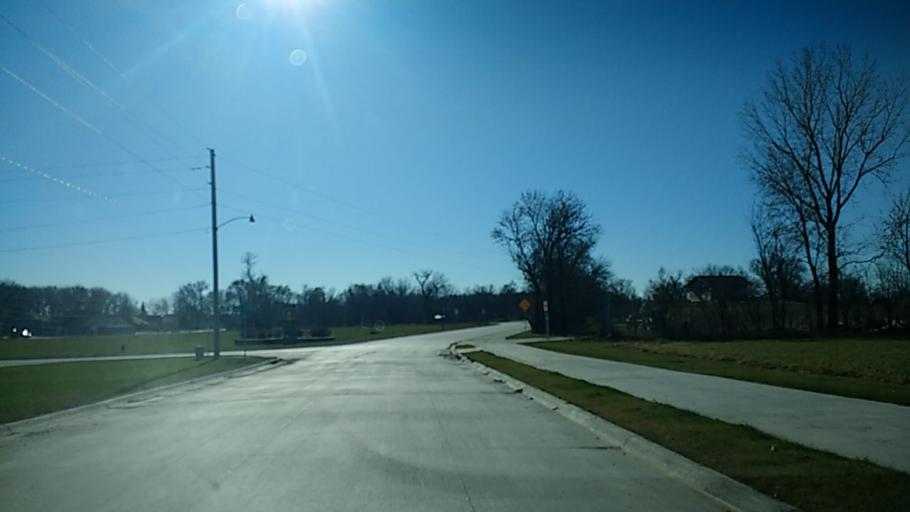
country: US
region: South Dakota
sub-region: Union County
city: North Sioux City
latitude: 42.5422
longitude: -96.5266
